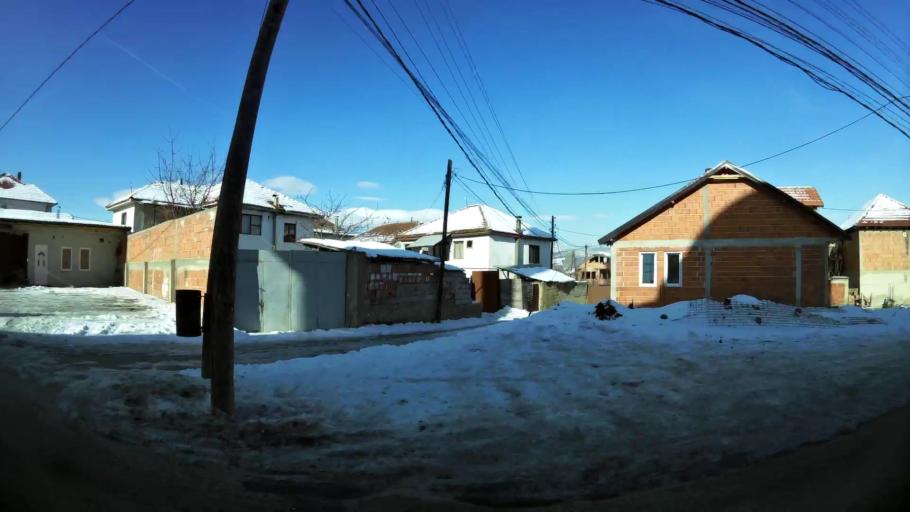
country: MK
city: Grchec
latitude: 41.9952
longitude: 21.3420
